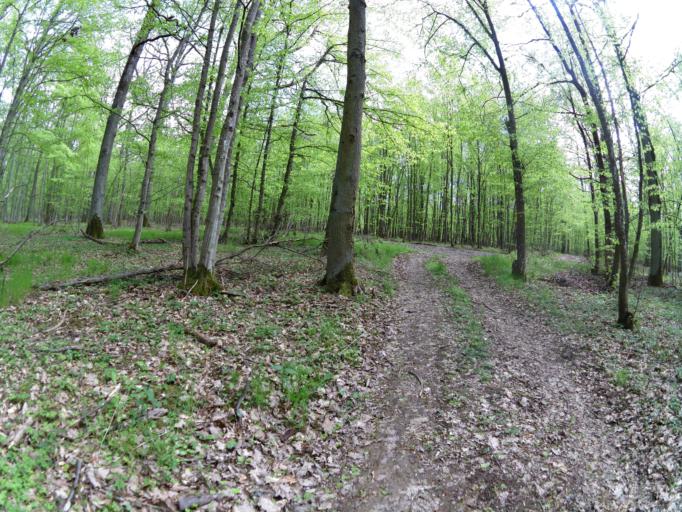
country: DE
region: Bavaria
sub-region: Regierungsbezirk Unterfranken
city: Prosselsheim
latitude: 49.8496
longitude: 10.1544
